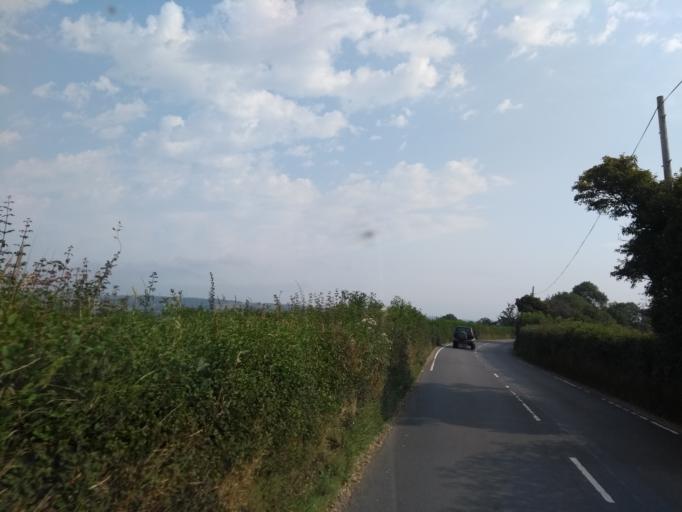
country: GB
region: England
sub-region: Devon
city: Axminster
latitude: 50.7617
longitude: -3.0146
